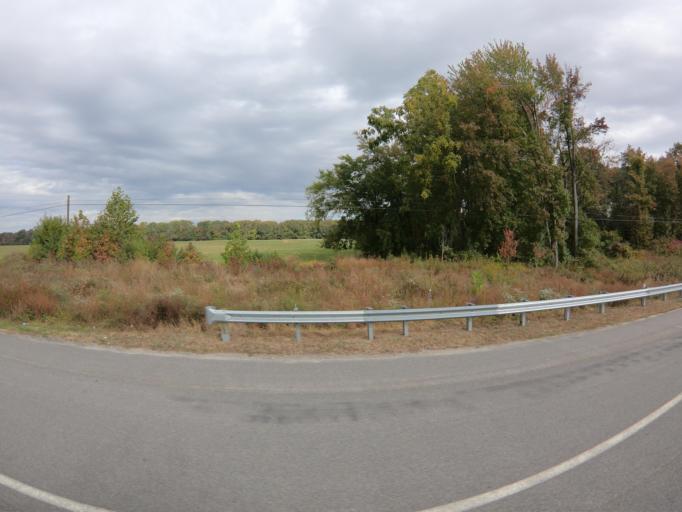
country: US
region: Maryland
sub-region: Queen Anne's County
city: Centreville
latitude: 38.9322
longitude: -76.0238
